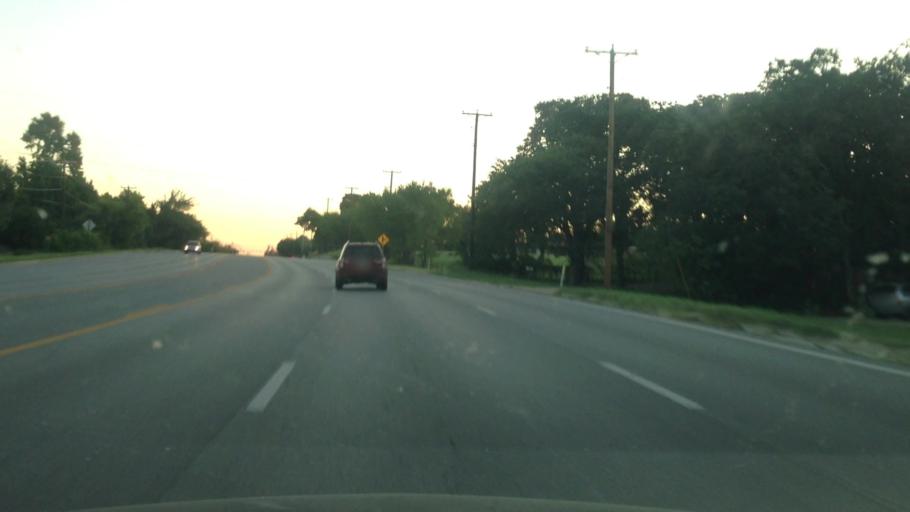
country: US
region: Texas
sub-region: Tarrant County
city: Colleyville
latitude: 32.8970
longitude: -97.1985
